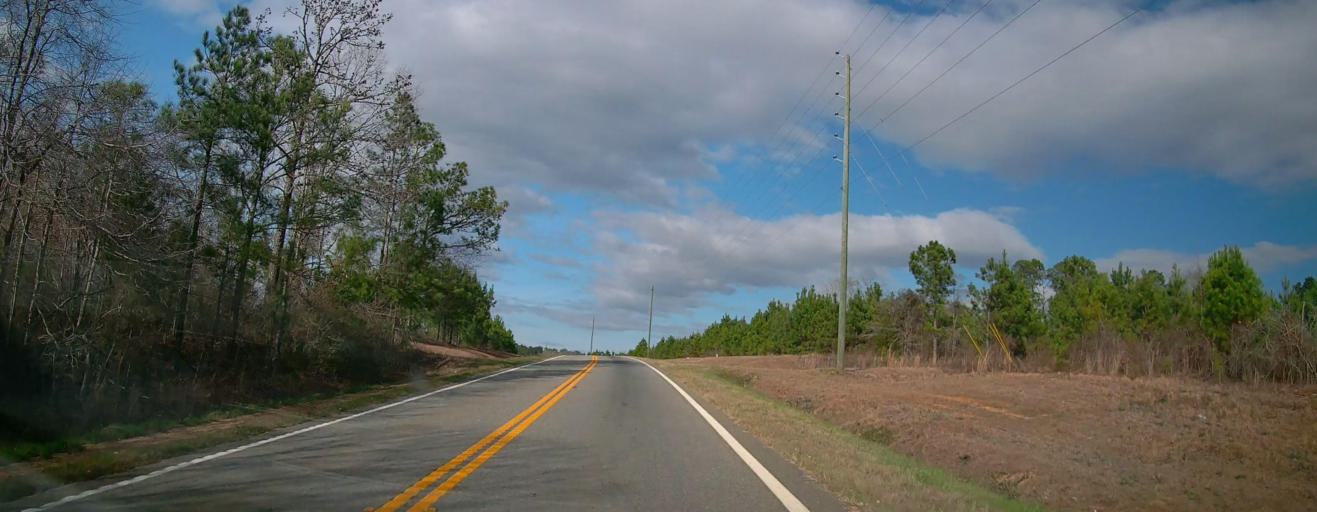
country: US
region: Georgia
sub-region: Taylor County
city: Butler
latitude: 32.4532
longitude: -84.3610
